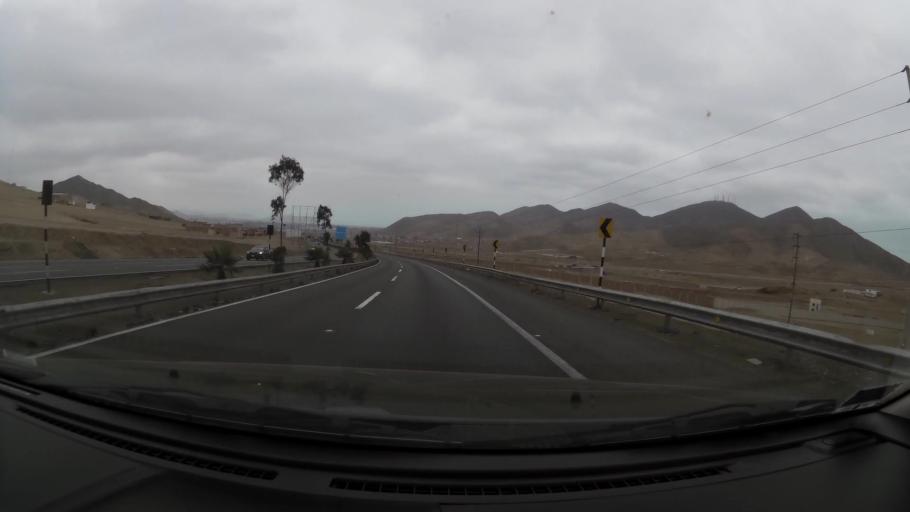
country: PE
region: Lima
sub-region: Lima
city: Pucusana
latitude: -12.4436
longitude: -76.7571
